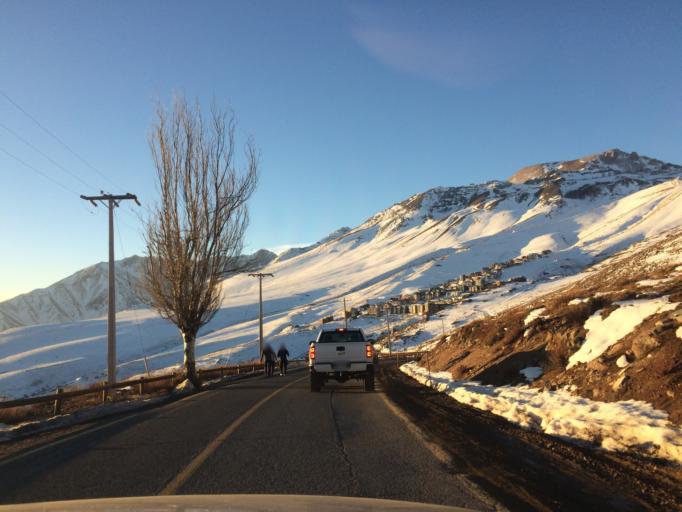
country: CL
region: Santiago Metropolitan
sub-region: Provincia de Santiago
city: Villa Presidente Frei, Nunoa, Santiago, Chile
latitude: -33.3488
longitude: -70.2962
